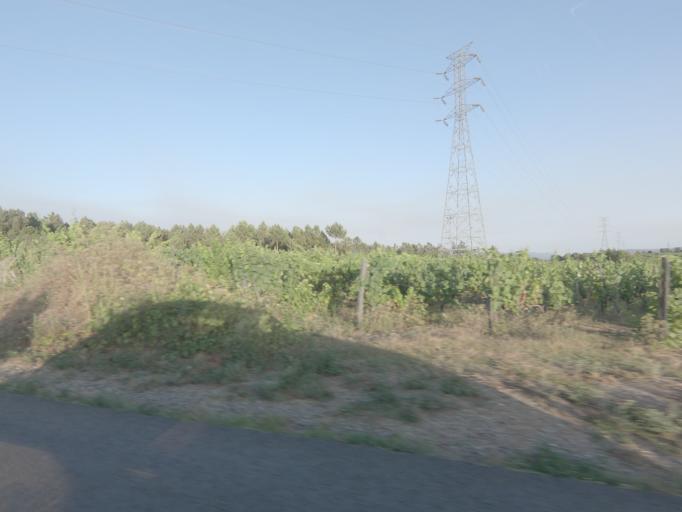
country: PT
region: Vila Real
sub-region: Sabrosa
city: Vilela
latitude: 41.2047
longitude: -7.6767
